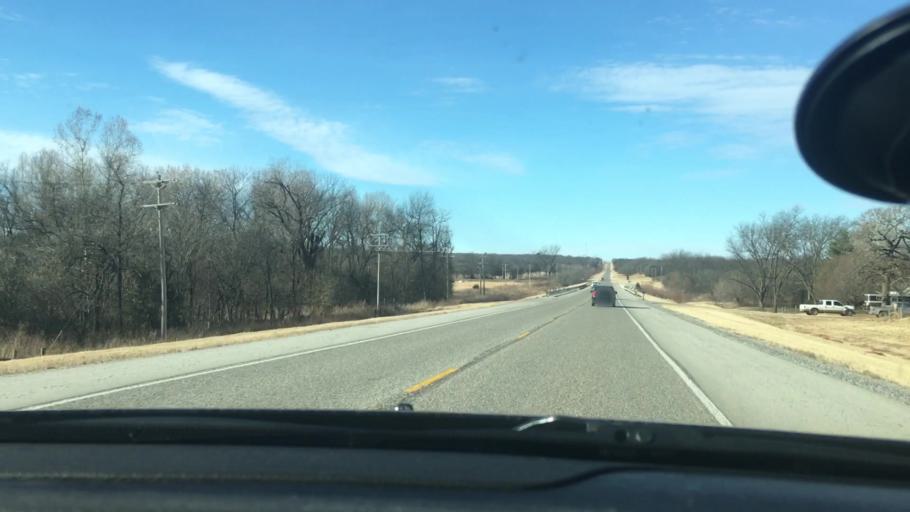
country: US
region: Oklahoma
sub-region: Cleveland County
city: Lexington
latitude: 35.0149
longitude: -97.1437
